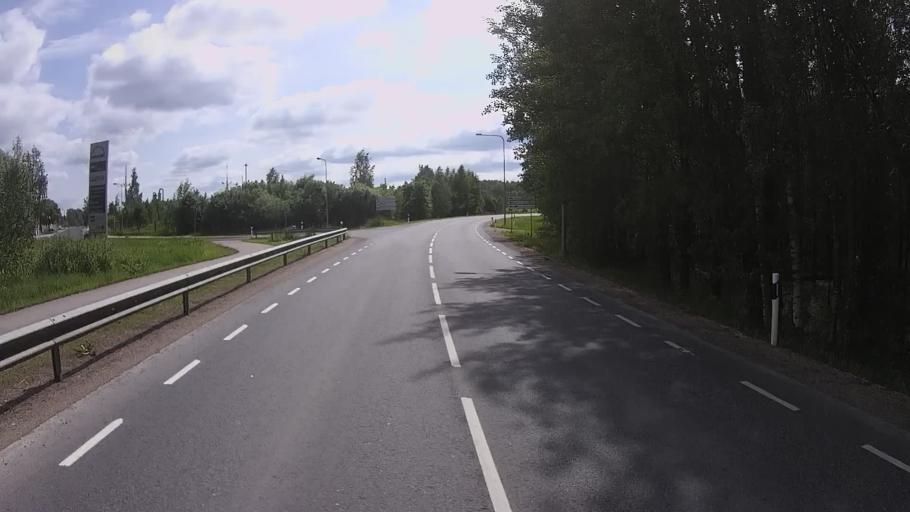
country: EE
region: Polvamaa
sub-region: Polva linn
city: Polva
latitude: 58.0658
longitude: 27.0792
